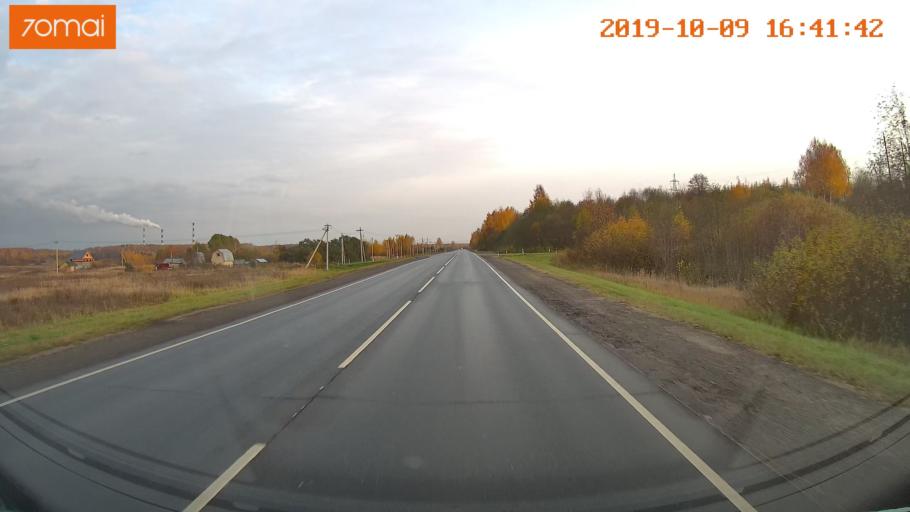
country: RU
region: Kostroma
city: Volgorechensk
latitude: 57.4702
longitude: 41.0862
